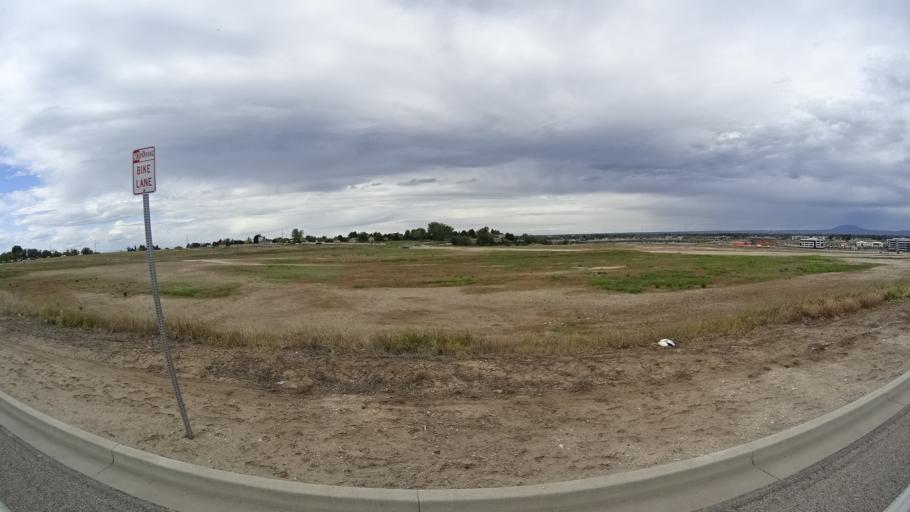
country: US
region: Idaho
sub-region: Ada County
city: Meridian
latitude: 43.5862
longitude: -116.4288
